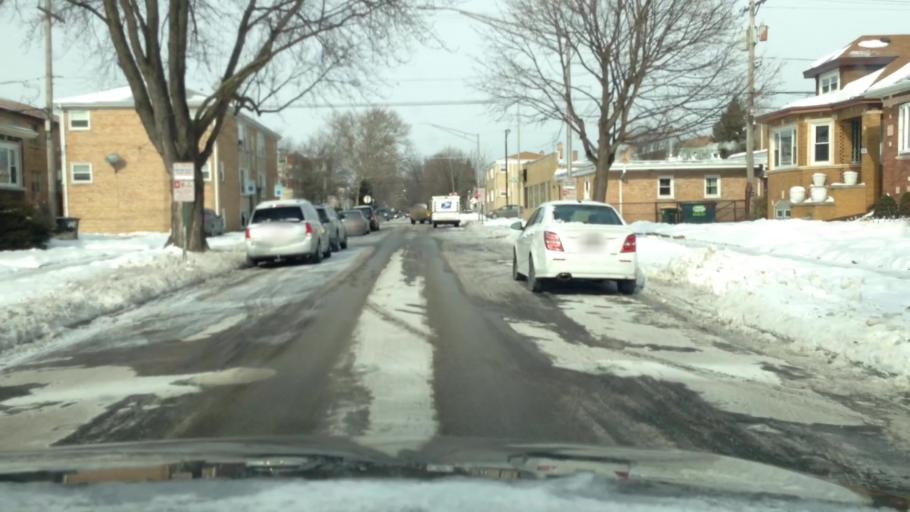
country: US
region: Illinois
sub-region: Cook County
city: River Grove
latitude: 41.9370
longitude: -87.8214
